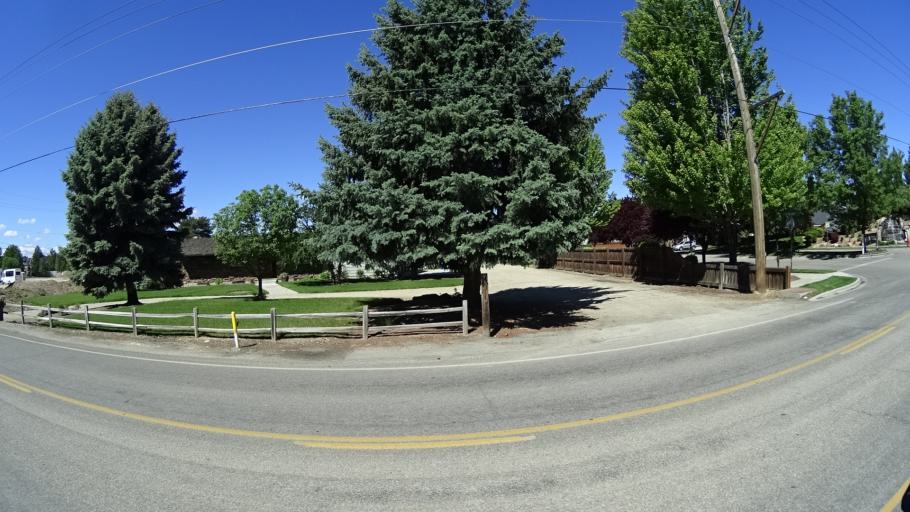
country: US
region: Idaho
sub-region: Ada County
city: Meridian
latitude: 43.6450
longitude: -116.3745
